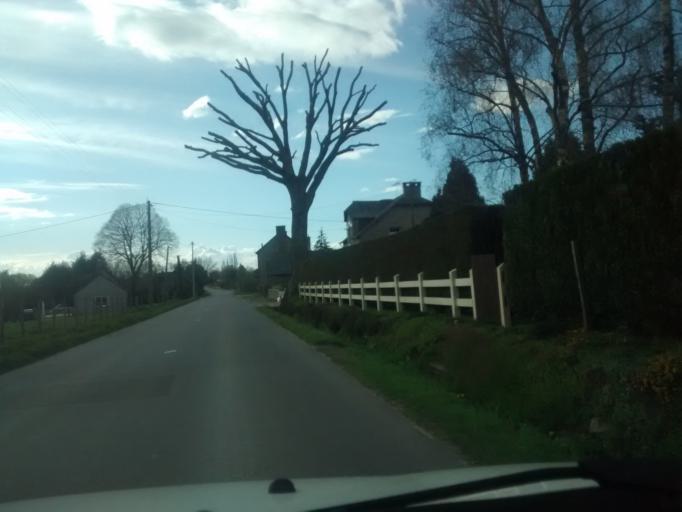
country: FR
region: Brittany
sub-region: Departement d'Ille-et-Vilaine
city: La Bouexiere
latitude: 48.1754
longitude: -1.4578
